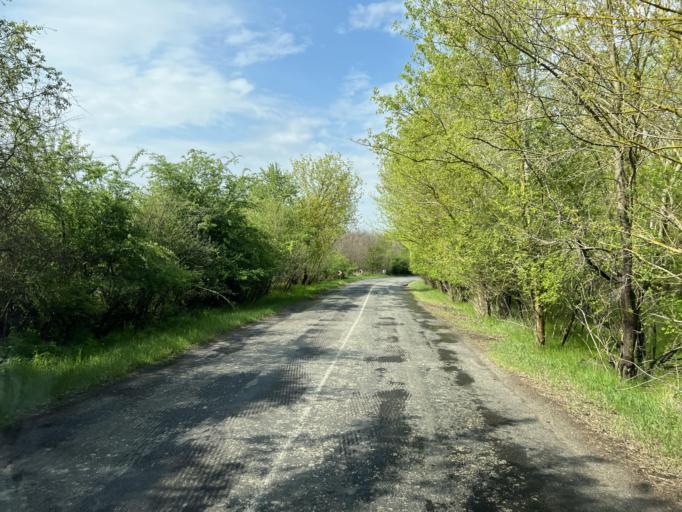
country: HU
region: Pest
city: Hernad
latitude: 47.1629
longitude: 19.4960
